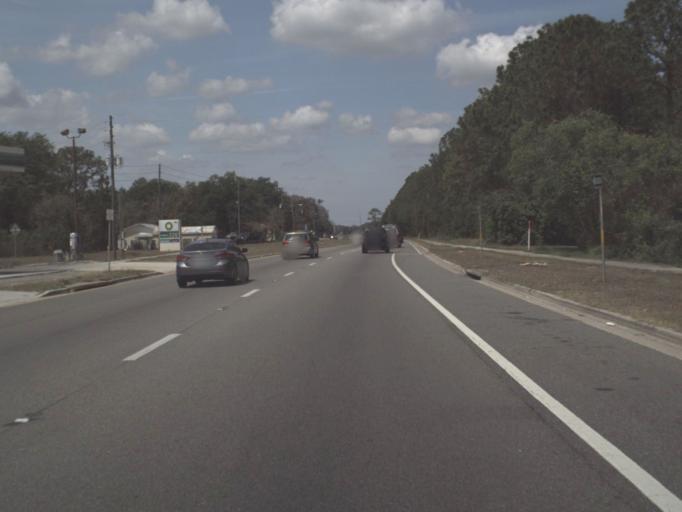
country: US
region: Florida
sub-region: Lake County
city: Groveland
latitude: 28.5624
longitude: -81.8597
